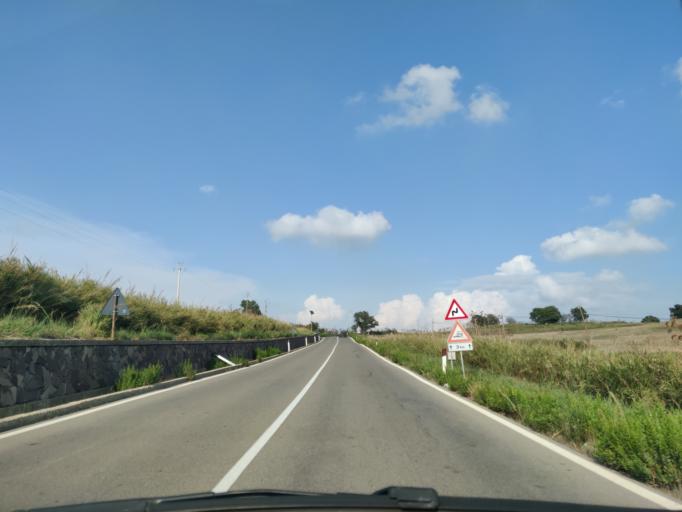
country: IT
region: Latium
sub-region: Provincia di Viterbo
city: Tarquinia
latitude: 42.2587
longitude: 11.8201
